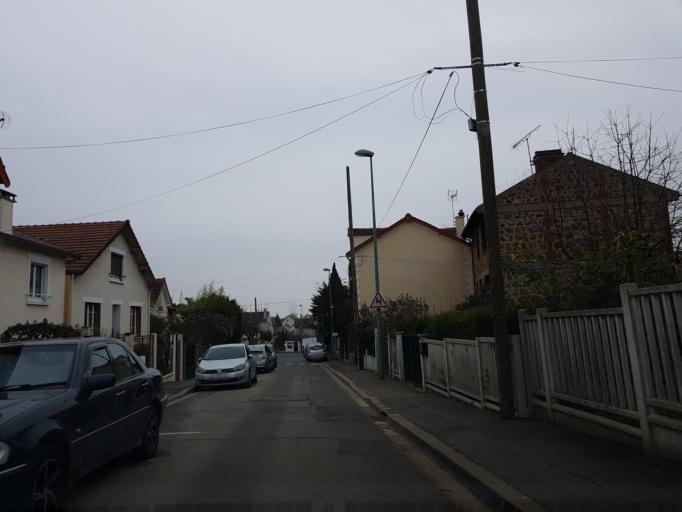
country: FR
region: Ile-de-France
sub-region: Departement du Val-de-Marne
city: Villejuif
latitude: 48.7949
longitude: 2.3778
